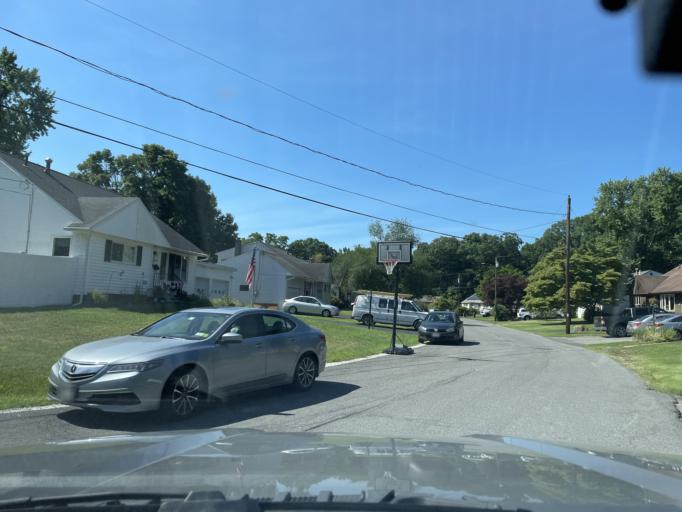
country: US
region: New York
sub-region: Ulster County
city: Saugerties South
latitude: 42.0651
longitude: -73.9606
